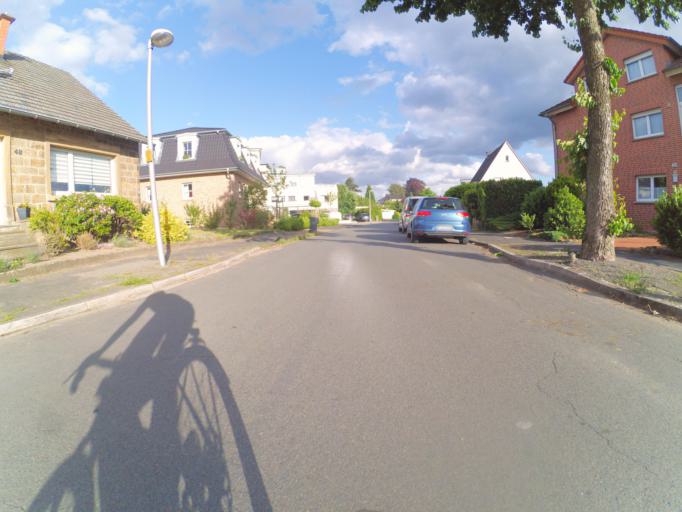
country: DE
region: North Rhine-Westphalia
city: Ibbenburen
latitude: 52.2770
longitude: 7.7072
